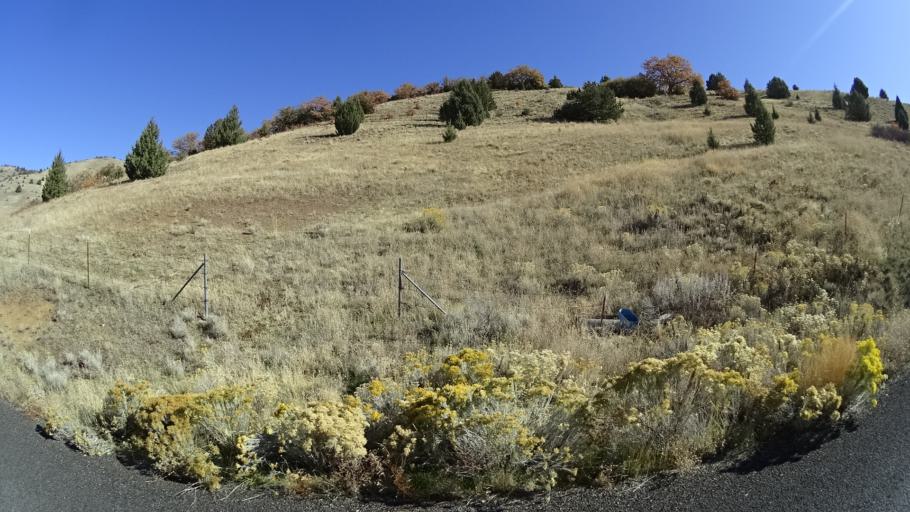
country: US
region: California
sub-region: Siskiyou County
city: Montague
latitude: 41.8278
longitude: -122.3435
